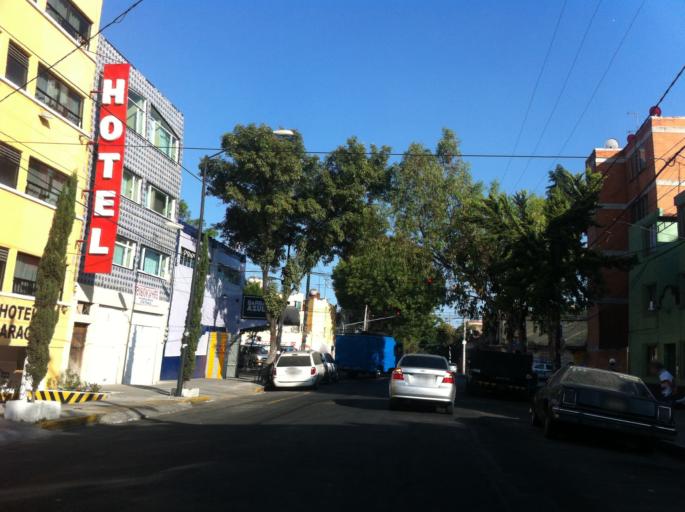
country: MX
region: Mexico City
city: Mexico City
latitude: 19.4158
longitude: -99.1415
